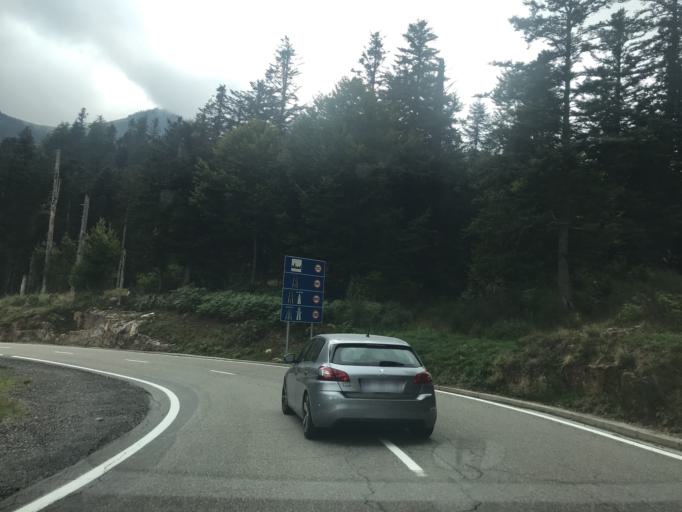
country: ES
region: Catalonia
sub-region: Provincia de Lleida
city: Les
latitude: 42.7685
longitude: 0.6595
